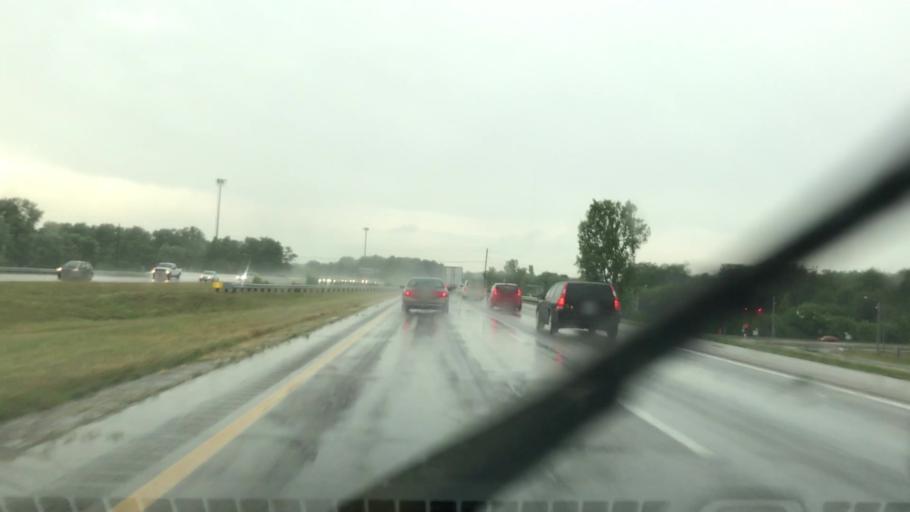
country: US
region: Ohio
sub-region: Clark County
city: Holiday Valley
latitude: 39.8439
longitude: -83.9930
